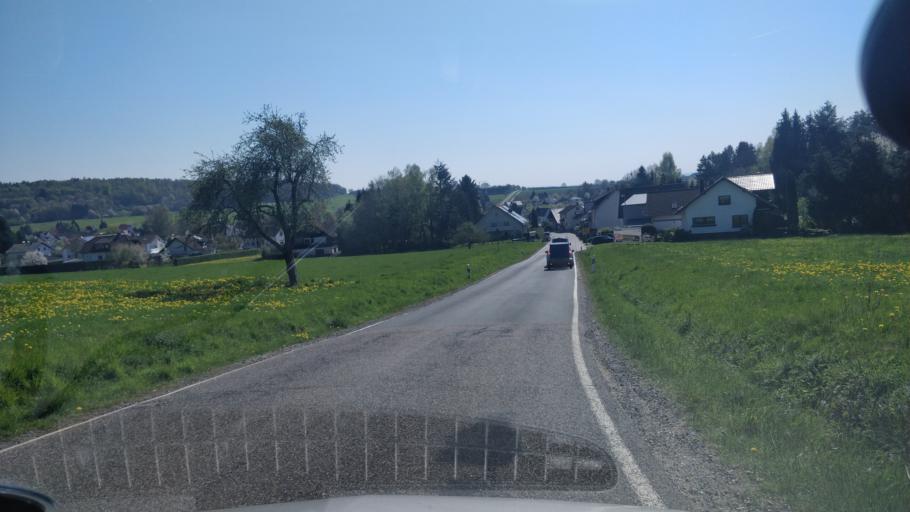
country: DE
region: Hesse
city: Waldbrunn
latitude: 50.5263
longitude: 8.0884
